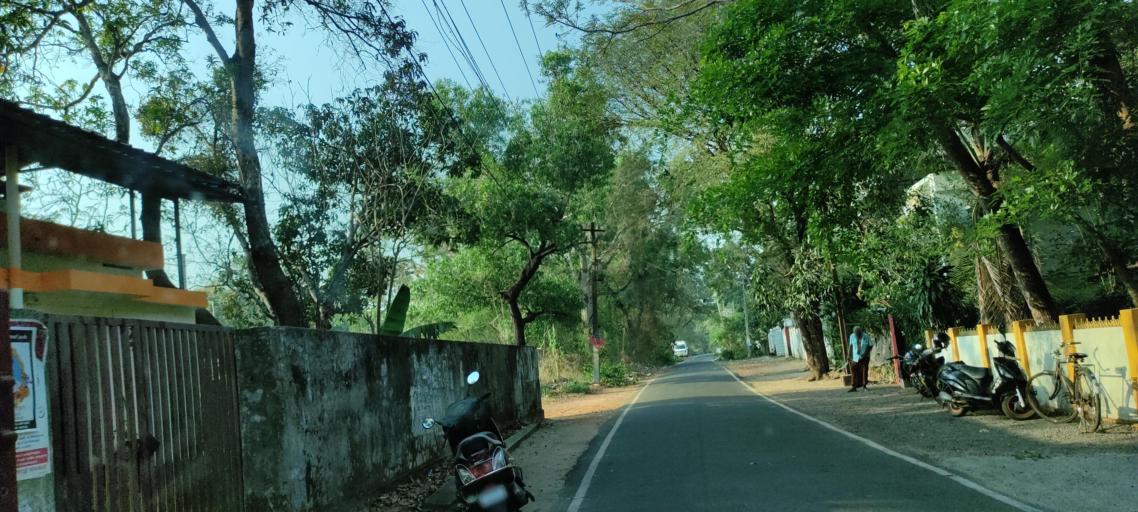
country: IN
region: Kerala
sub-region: Alappuzha
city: Alleppey
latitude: 9.5179
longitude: 76.3220
